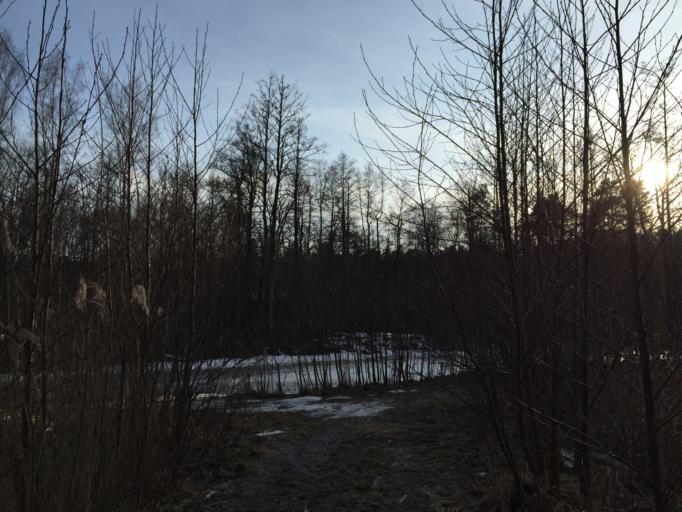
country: LV
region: Stopini
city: Ulbroka
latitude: 56.9592
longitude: 24.2857
